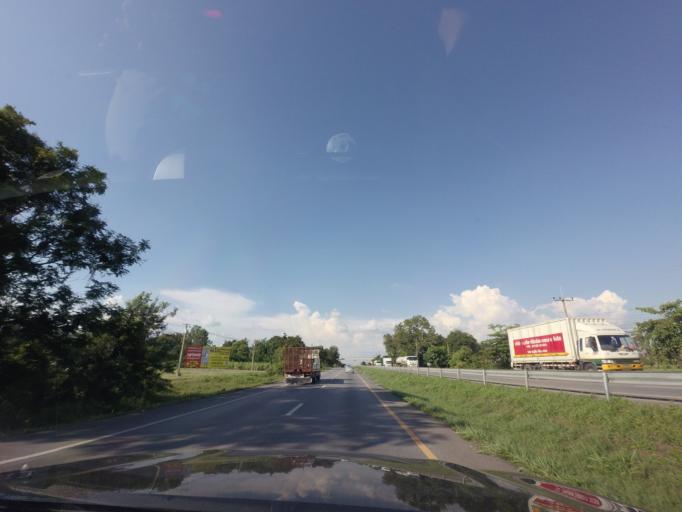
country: TH
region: Khon Kaen
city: Non Sila
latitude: 15.9745
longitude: 102.6939
